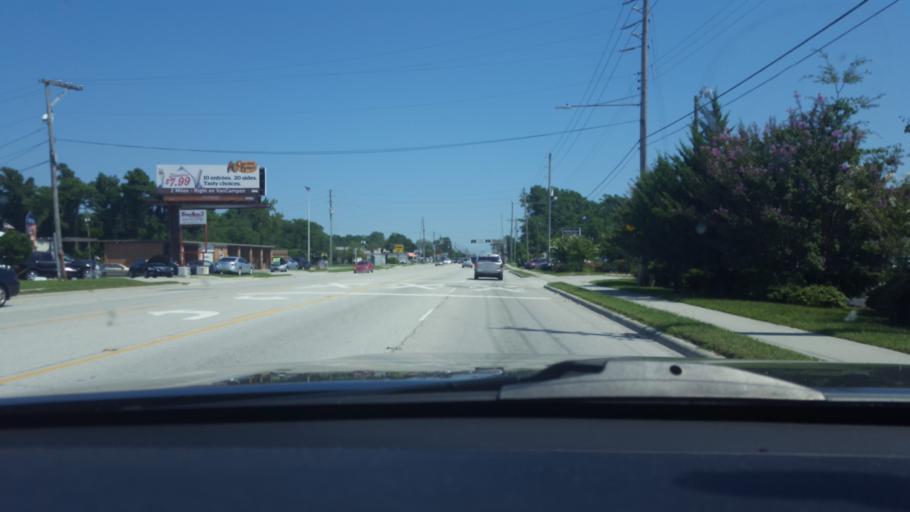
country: US
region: North Carolina
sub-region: New Hanover County
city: Kings Grant
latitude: 34.2408
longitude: -77.9015
